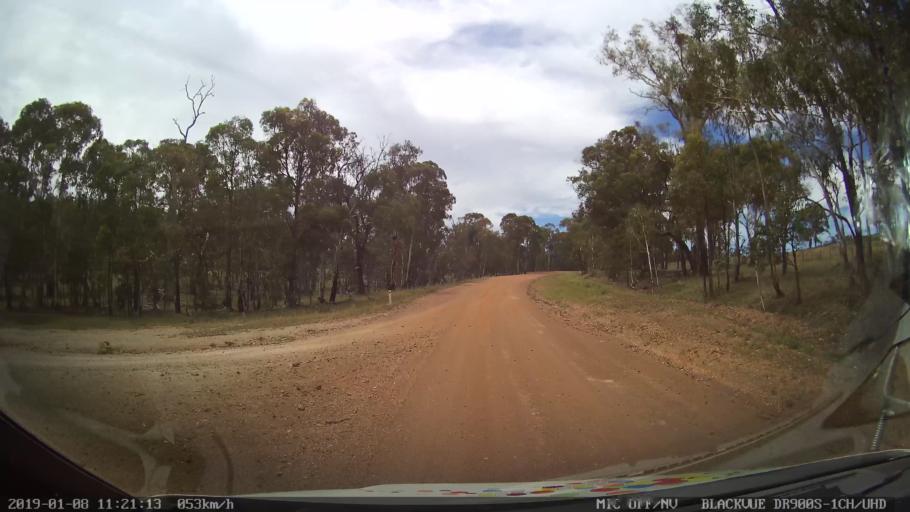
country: AU
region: New South Wales
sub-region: Guyra
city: Guyra
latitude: -30.2357
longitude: 151.5658
